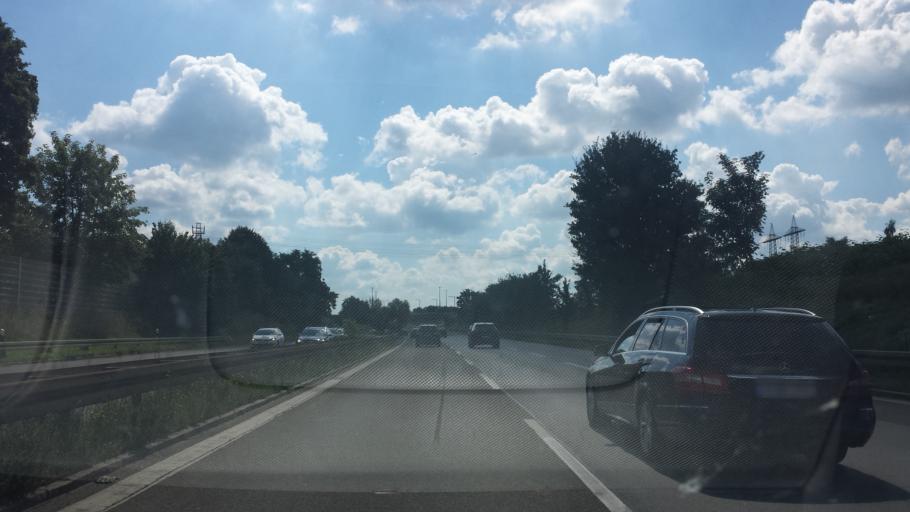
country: DE
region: Bavaria
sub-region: Regierungsbezirk Mittelfranken
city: Grossreuth bei Schweinau
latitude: 49.4159
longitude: 11.0584
